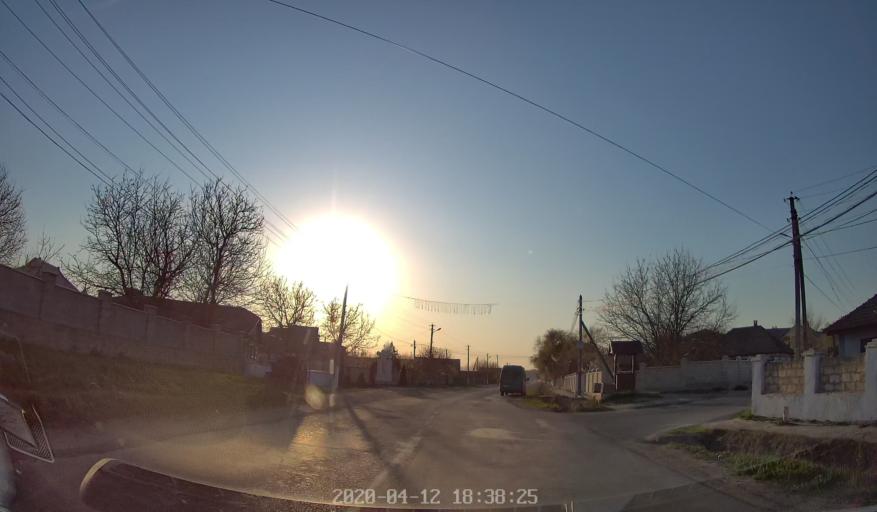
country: MD
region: Chisinau
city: Vadul lui Voda
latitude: 47.1242
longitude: 29.0011
